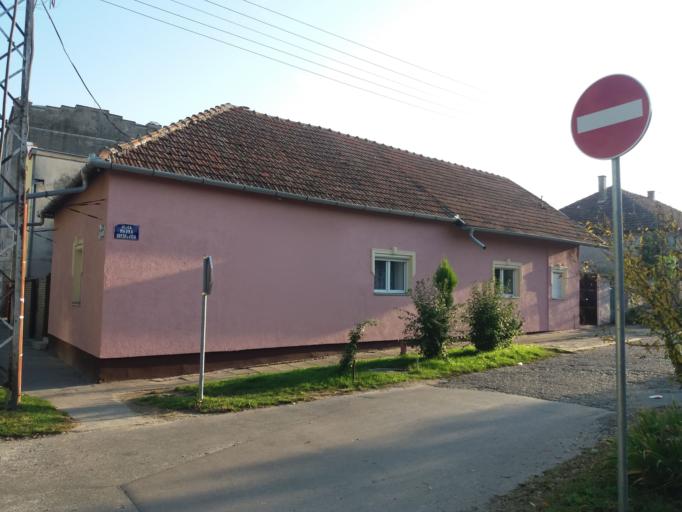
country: RS
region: Autonomna Pokrajina Vojvodina
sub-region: Severnobacki Okrug
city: Subotica
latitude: 46.0951
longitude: 19.6640
